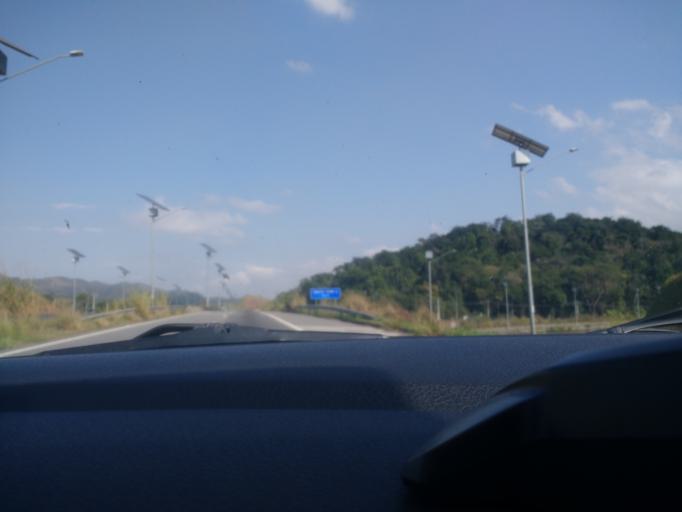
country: BR
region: Rio de Janeiro
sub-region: Nova Iguacu
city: Nova Iguacu
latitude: -22.6832
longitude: -43.4773
